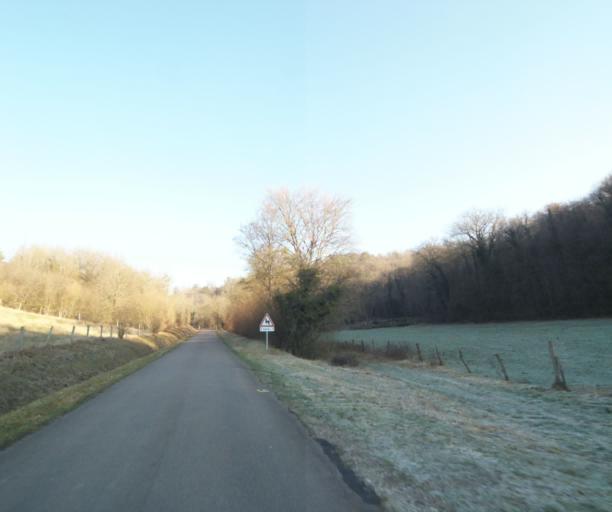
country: FR
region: Champagne-Ardenne
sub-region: Departement de la Haute-Marne
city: Chevillon
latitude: 48.5389
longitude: 5.1145
